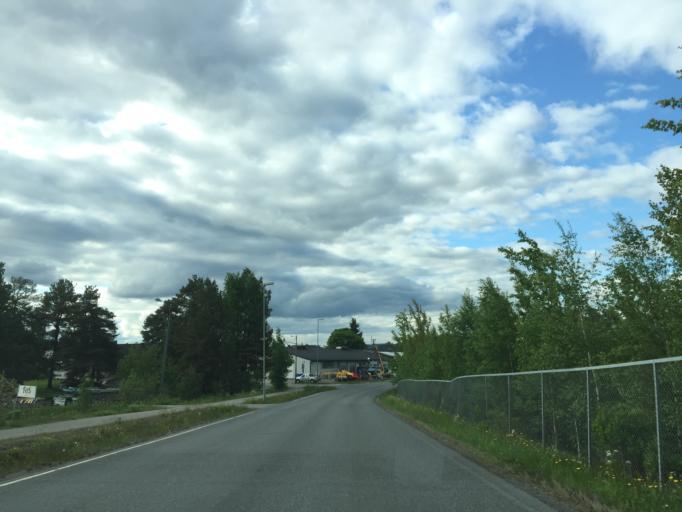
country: NO
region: Akershus
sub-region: Raelingen
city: Fjerdingby
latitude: 59.9508
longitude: 11.0753
